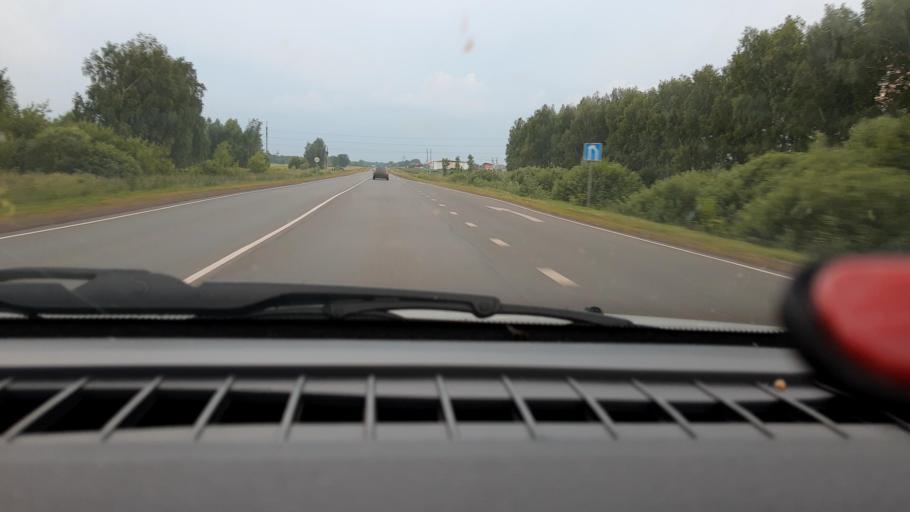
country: RU
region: Nizjnij Novgorod
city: Arzamas
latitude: 55.3034
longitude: 43.9214
